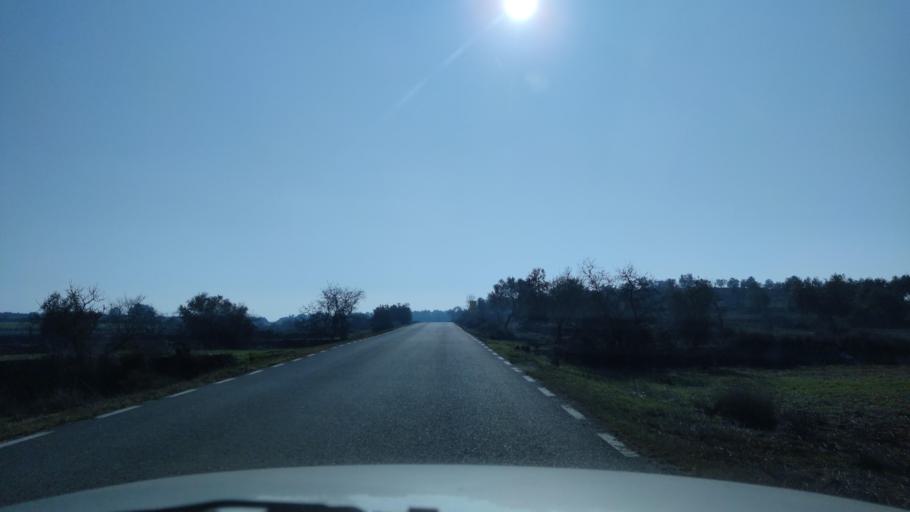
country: ES
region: Catalonia
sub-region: Provincia de Lleida
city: Torrebesses
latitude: 41.4707
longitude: 0.5619
